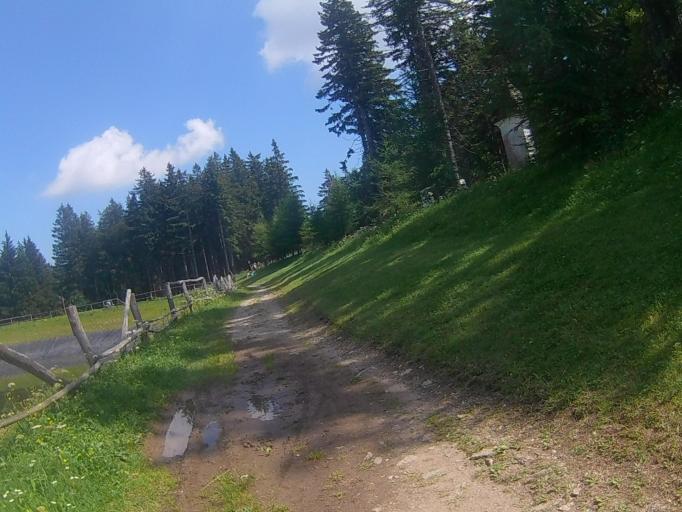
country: SI
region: Ruse
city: Ruse
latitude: 46.4954
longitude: 15.5124
